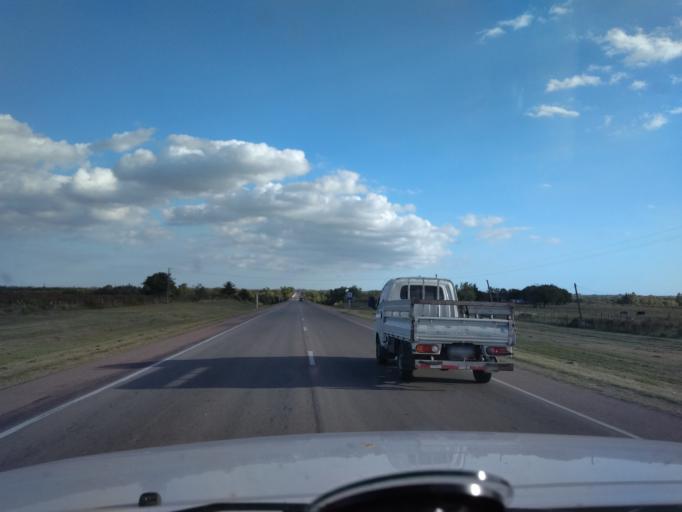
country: UY
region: Florida
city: Cardal
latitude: -34.3547
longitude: -56.2483
